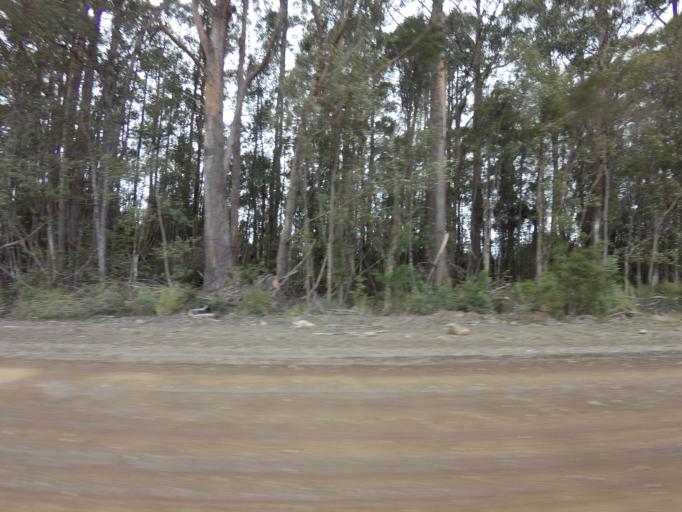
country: AU
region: Tasmania
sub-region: Huon Valley
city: Geeveston
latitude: -43.4880
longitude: 146.8911
